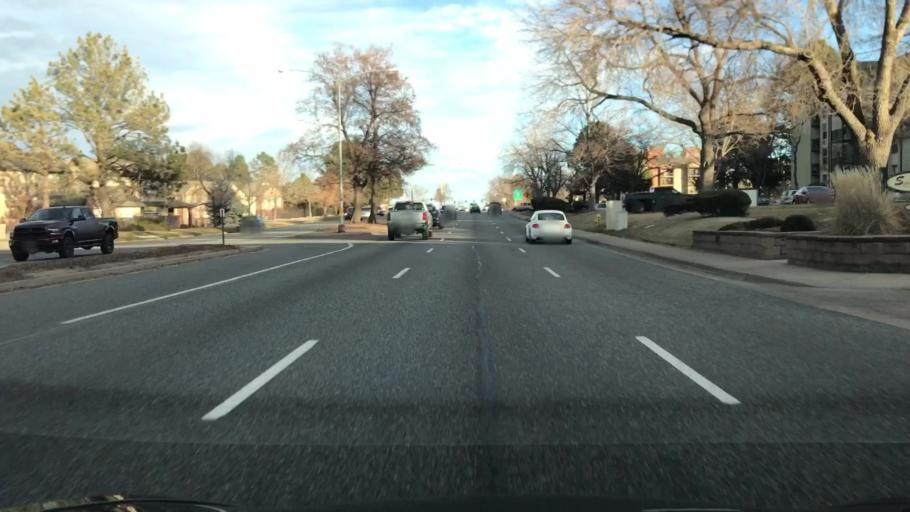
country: US
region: Colorado
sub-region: Adams County
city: Aurora
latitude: 39.6750
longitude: -104.8366
